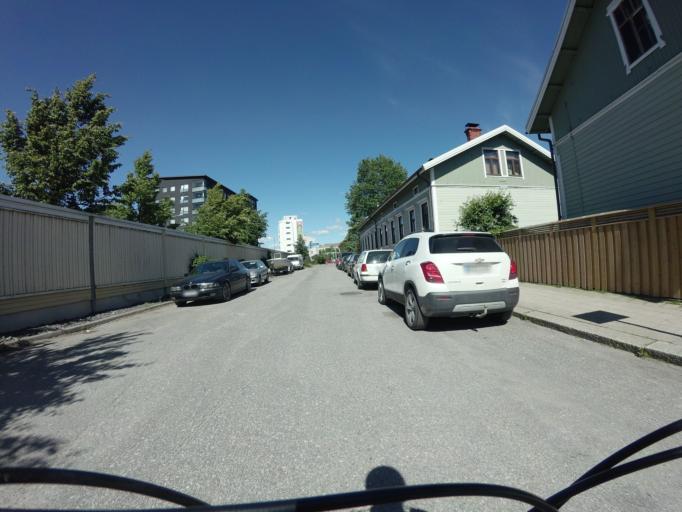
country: FI
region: Varsinais-Suomi
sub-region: Turku
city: Turku
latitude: 60.4501
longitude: 22.2447
